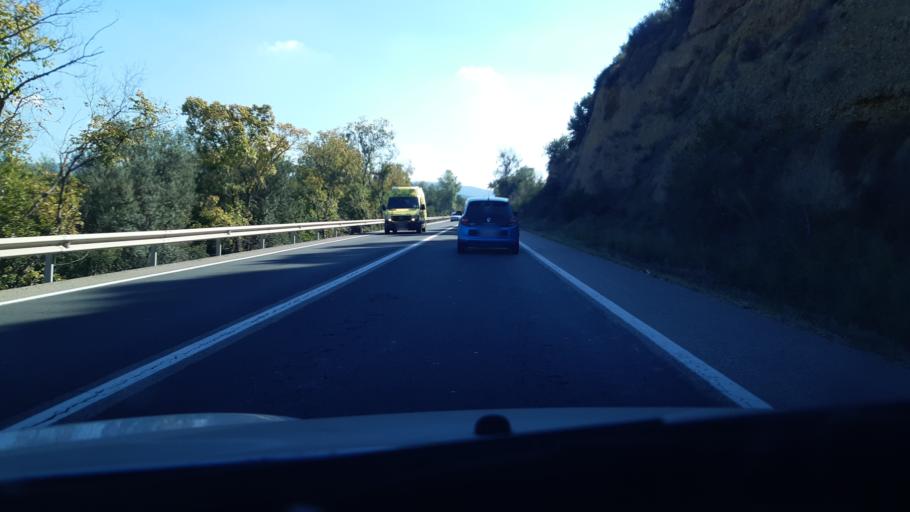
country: ES
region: Catalonia
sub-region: Provincia de Tarragona
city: Tivenys
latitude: 40.8604
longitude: 0.5095
